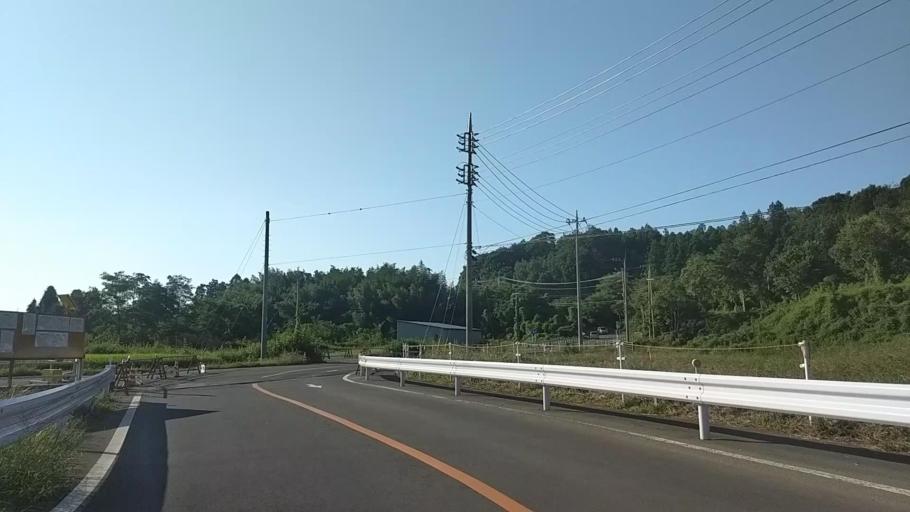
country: JP
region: Gunma
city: Annaka
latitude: 36.3393
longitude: 138.8882
